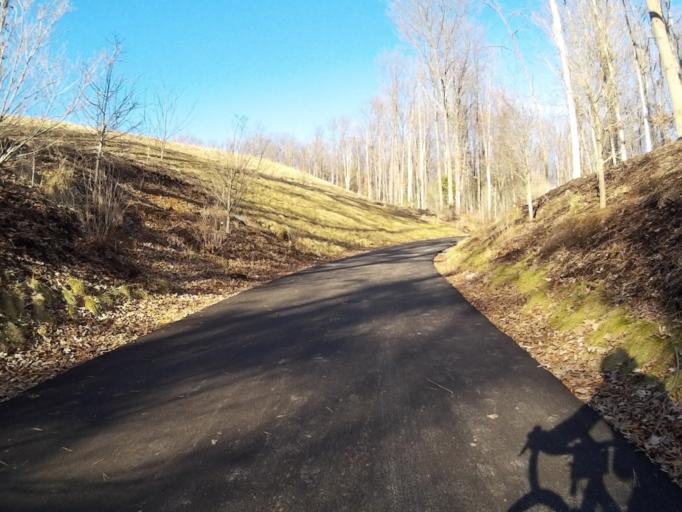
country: US
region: Pennsylvania
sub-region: Centre County
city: State College
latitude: 40.8209
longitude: -77.8827
